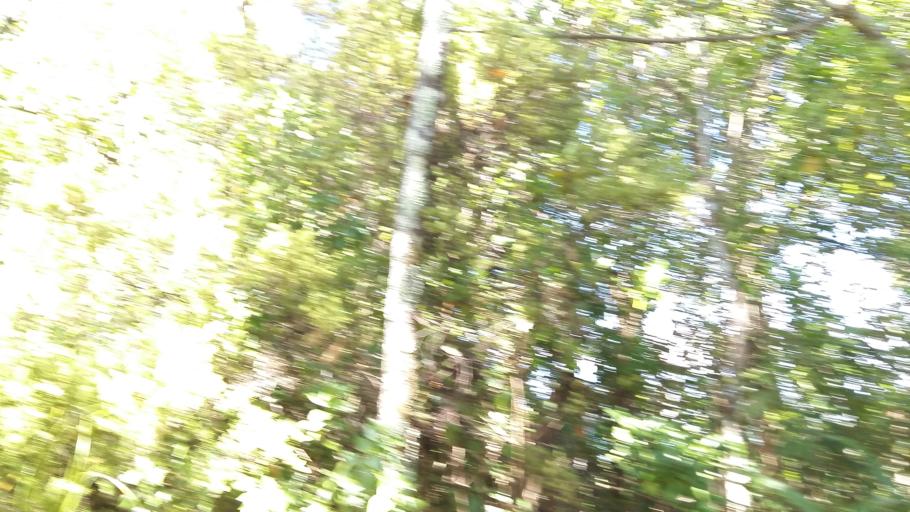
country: NZ
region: Bay of Plenty
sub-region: Whakatane District
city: Whakatane
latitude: -37.9432
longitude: 177.0141
